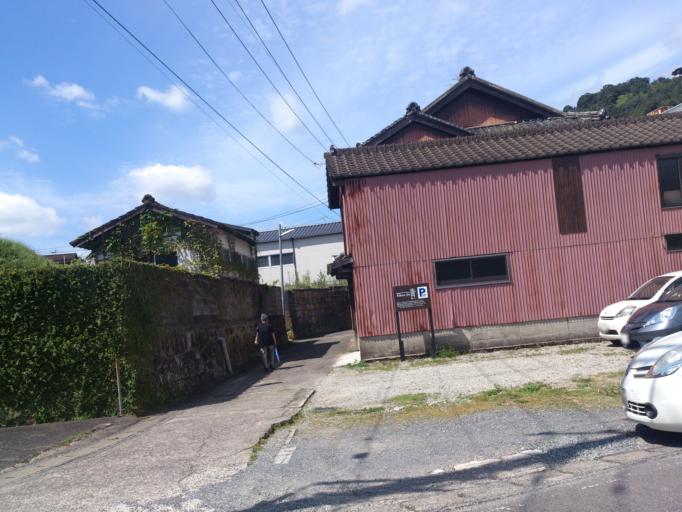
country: JP
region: Saga Prefecture
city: Imaricho-ko
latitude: 33.1914
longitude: 129.9034
